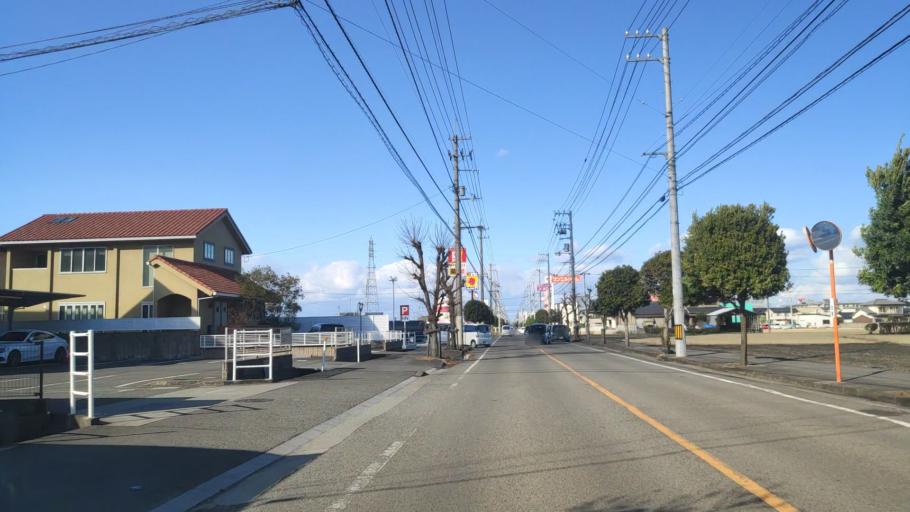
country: JP
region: Ehime
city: Saijo
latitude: 33.9236
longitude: 133.1913
